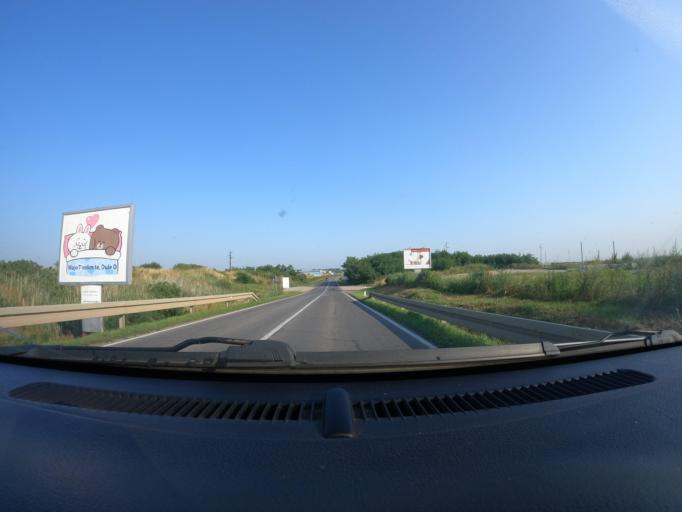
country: RS
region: Autonomna Pokrajina Vojvodina
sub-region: Sremski Okrug
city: Ingija
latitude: 45.0216
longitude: 20.1112
